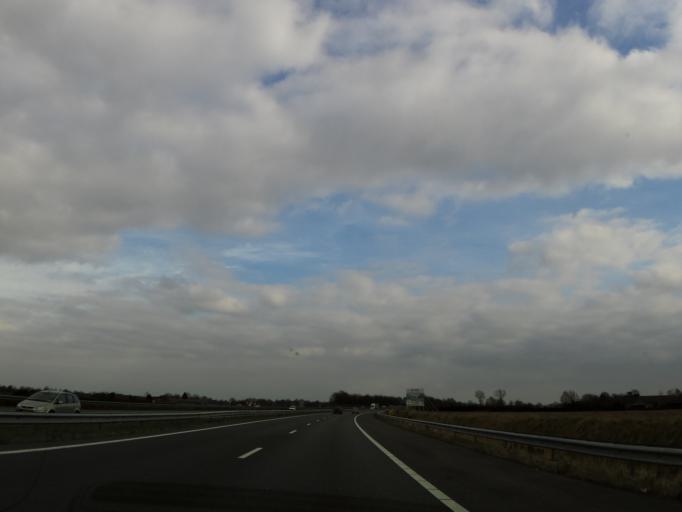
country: NL
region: Limburg
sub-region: Gemeente Nederweert
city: Nederweert
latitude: 51.2820
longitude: 5.7255
